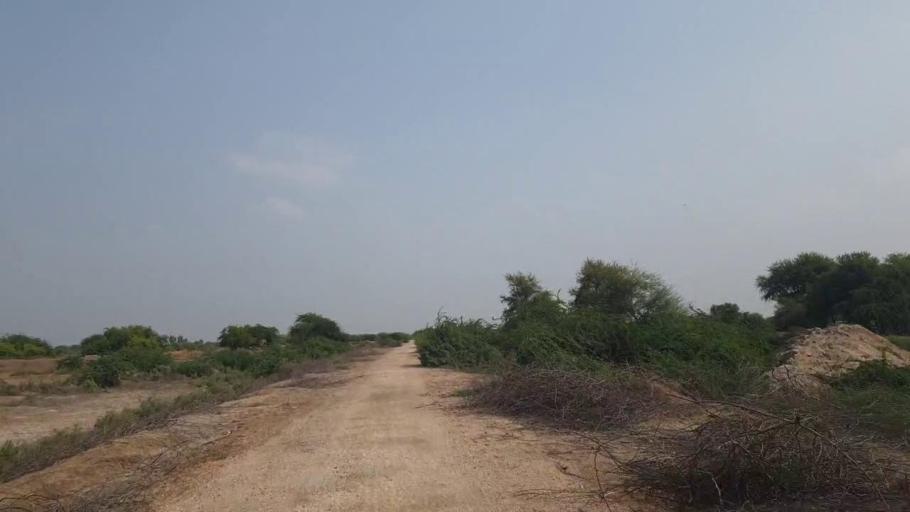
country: PK
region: Sindh
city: Badin
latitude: 24.5474
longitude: 68.7002
